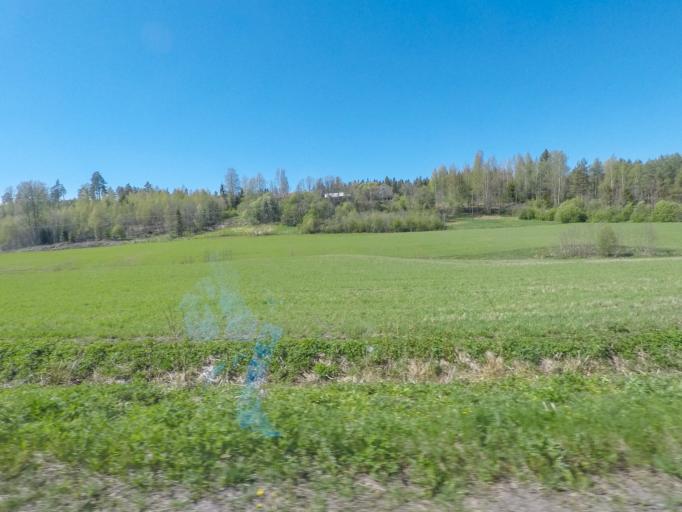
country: FI
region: Uusimaa
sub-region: Helsinki
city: Sammatti
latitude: 60.4120
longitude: 23.8240
